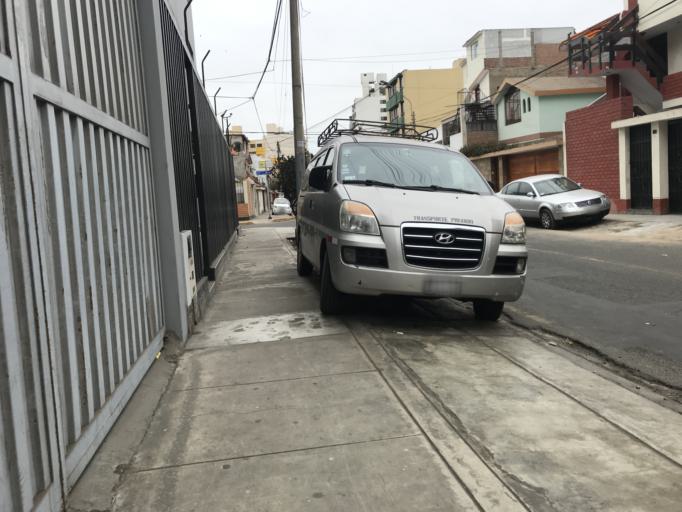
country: PE
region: Callao
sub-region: Callao
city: Callao
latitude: -12.0750
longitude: -77.0853
